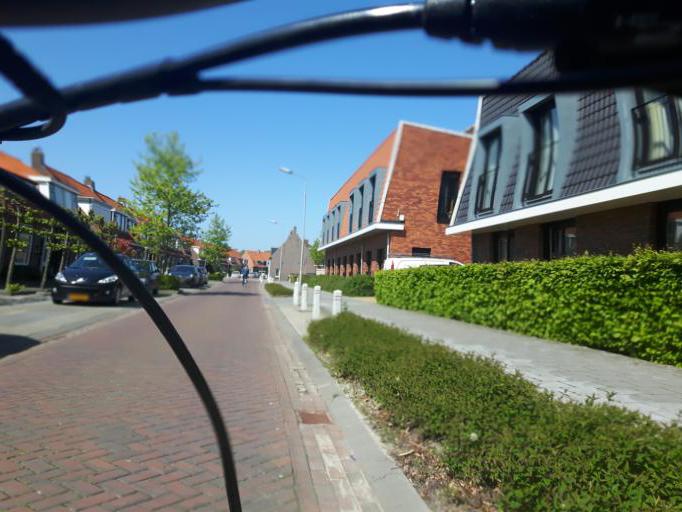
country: NL
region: Zeeland
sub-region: Gemeente Goes
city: Goes
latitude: 51.5021
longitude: 3.8839
